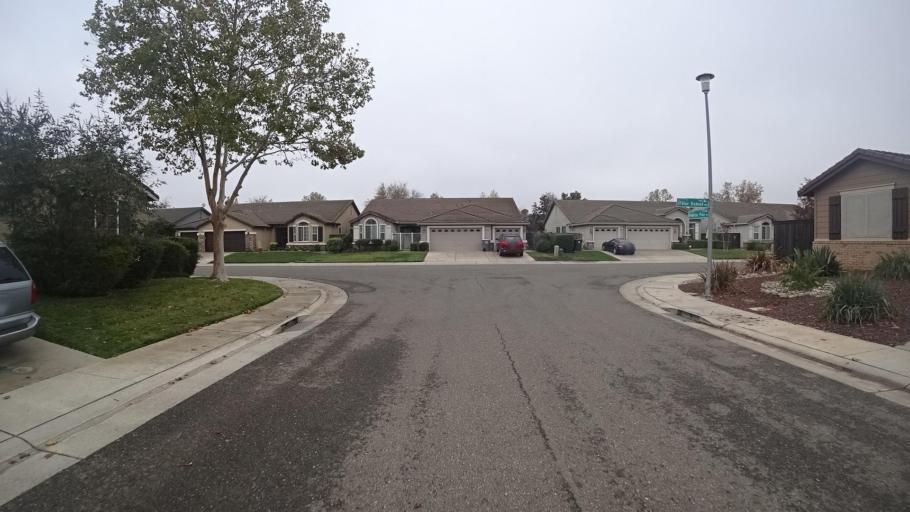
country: US
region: California
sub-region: Sacramento County
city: Elk Grove
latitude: 38.4031
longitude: -121.3452
